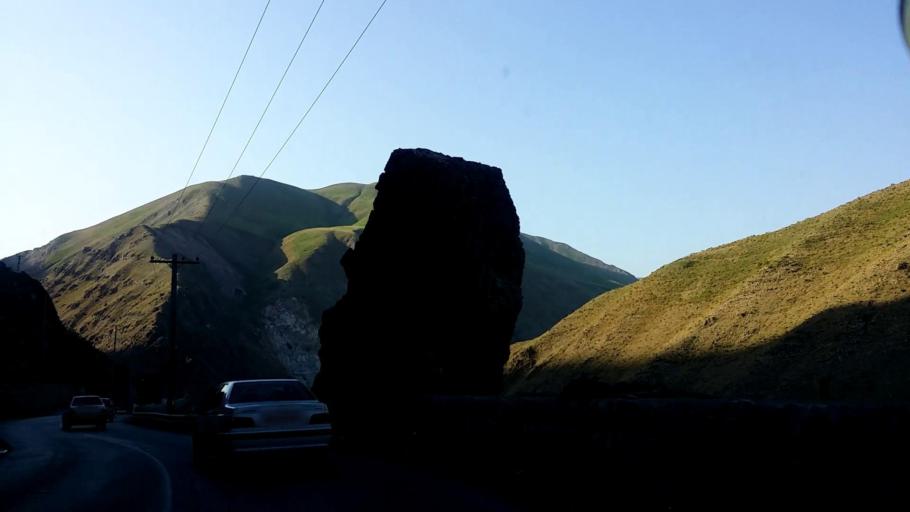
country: IR
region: Tehran
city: Tajrish
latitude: 36.1196
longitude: 51.3170
